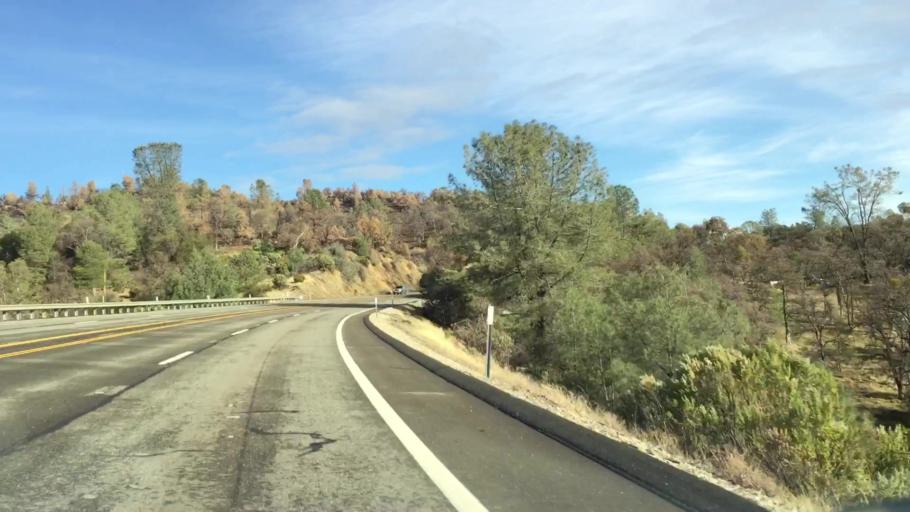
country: US
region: California
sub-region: Butte County
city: Paradise
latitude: 39.6847
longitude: -121.5395
